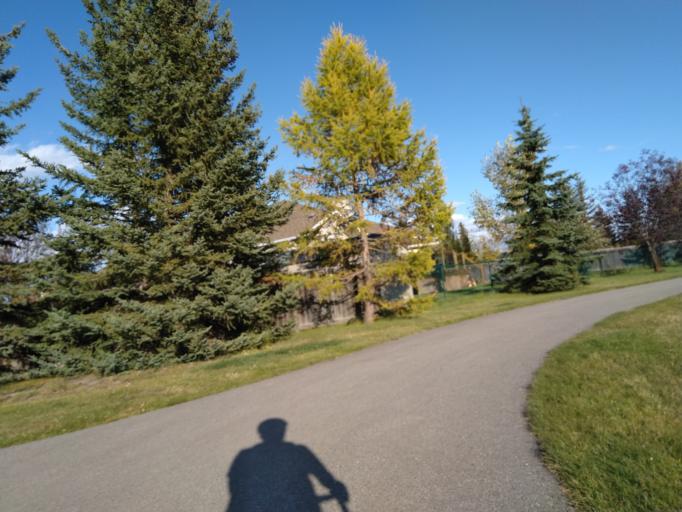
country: CA
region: Alberta
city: Cochrane
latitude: 51.1839
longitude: -114.4931
